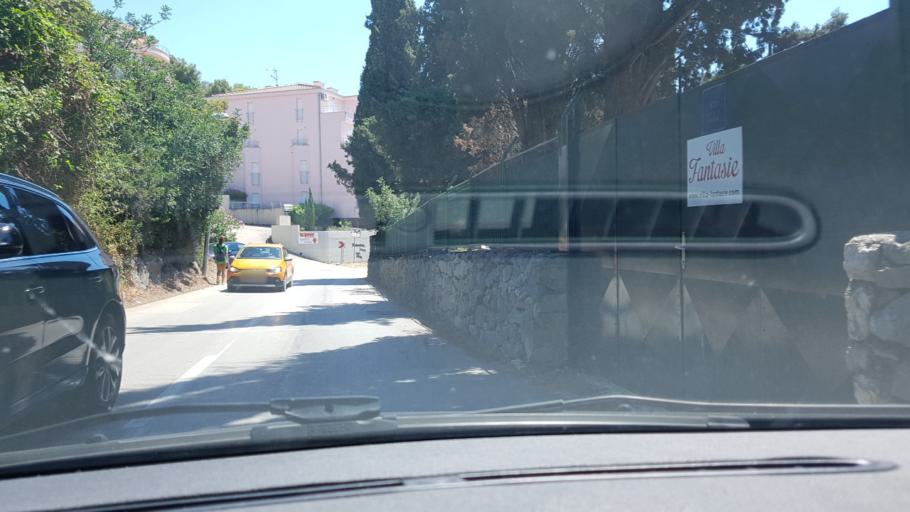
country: HR
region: Splitsko-Dalmatinska
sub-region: Grad Trogir
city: Trogir
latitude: 43.5108
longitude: 16.2540
